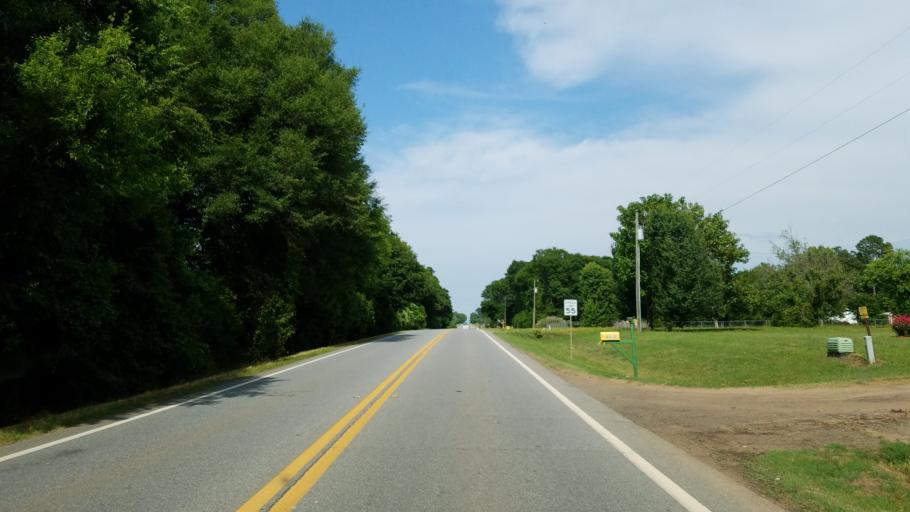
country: US
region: Georgia
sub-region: Houston County
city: Perry
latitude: 32.4402
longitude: -83.7877
